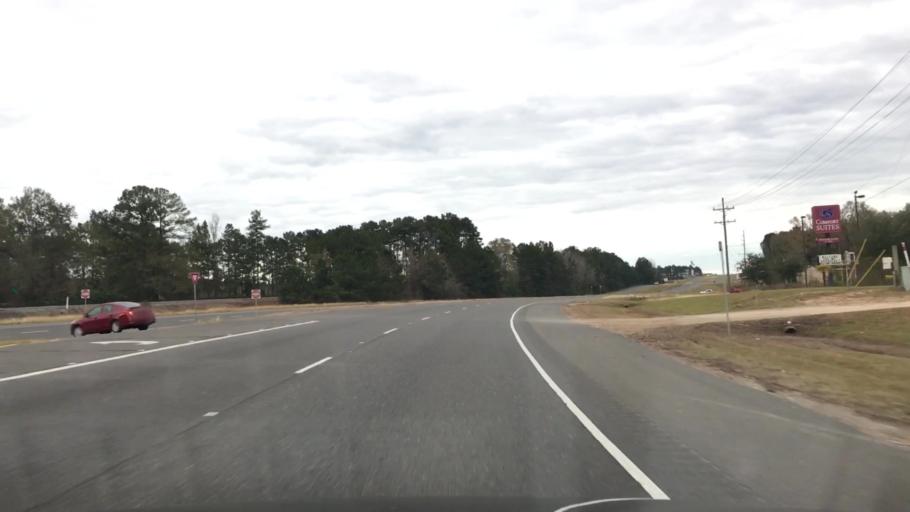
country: US
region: Louisiana
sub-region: Vernon Parish
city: New Llano
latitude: 31.1004
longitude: -93.2694
